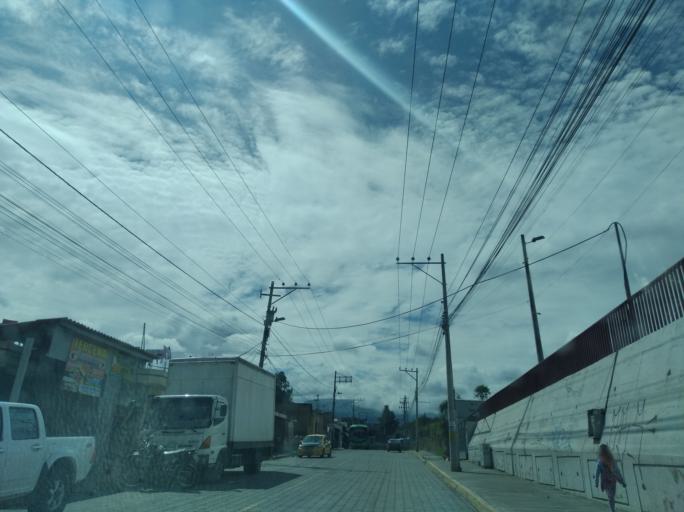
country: EC
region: Pichincha
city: Sangolqui
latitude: -0.2193
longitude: -78.3391
